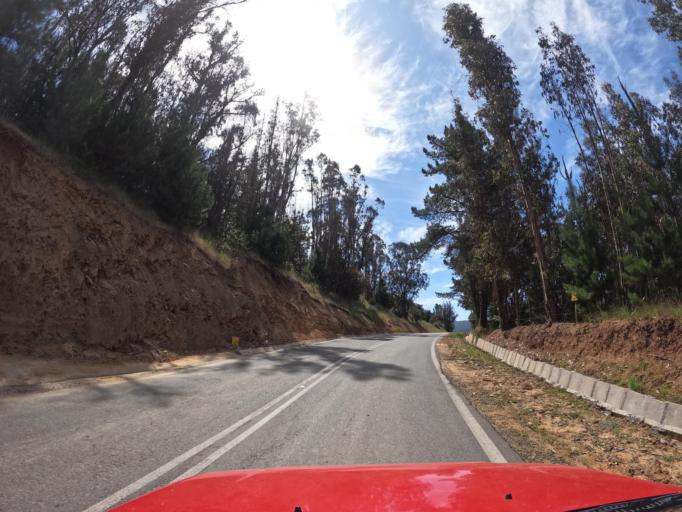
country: CL
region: Maule
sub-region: Provincia de Talca
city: Talca
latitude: -35.0100
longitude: -71.9726
